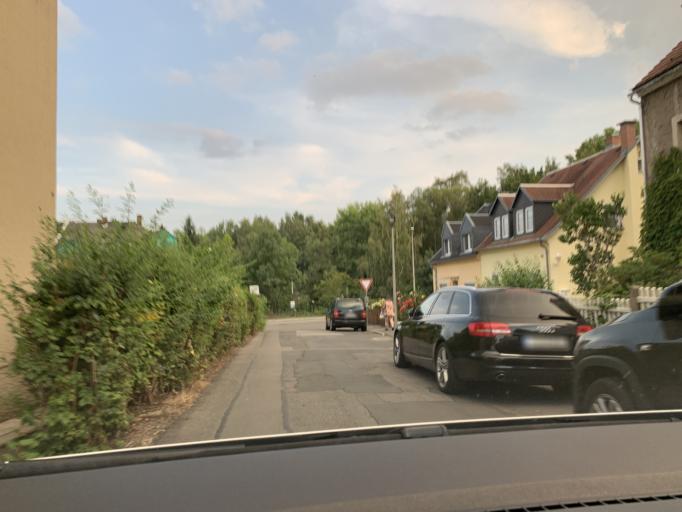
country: DE
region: Saxony
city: Freiberg
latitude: 50.9112
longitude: 13.3303
